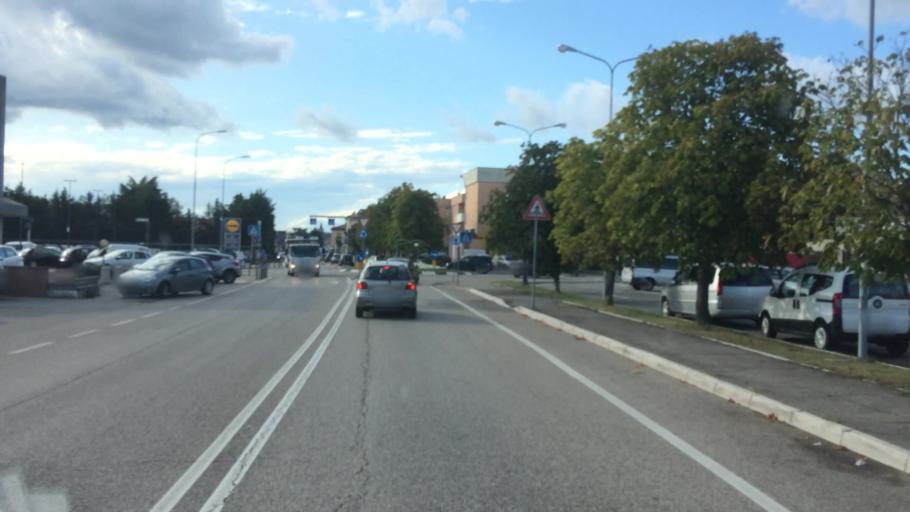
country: IT
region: Veneto
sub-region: Provincia di Verona
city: Bussolengo
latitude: 45.4683
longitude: 10.8622
